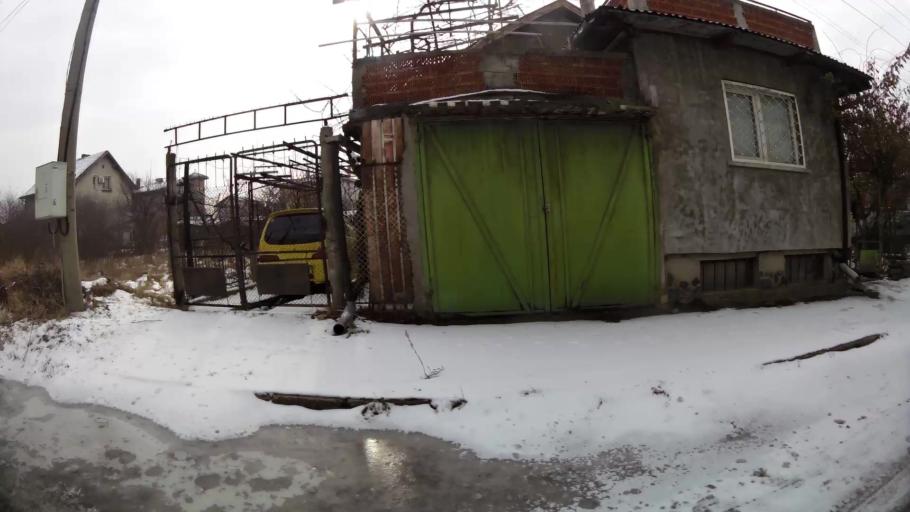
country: BG
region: Sofia-Capital
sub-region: Stolichna Obshtina
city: Sofia
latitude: 42.7068
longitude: 23.4124
